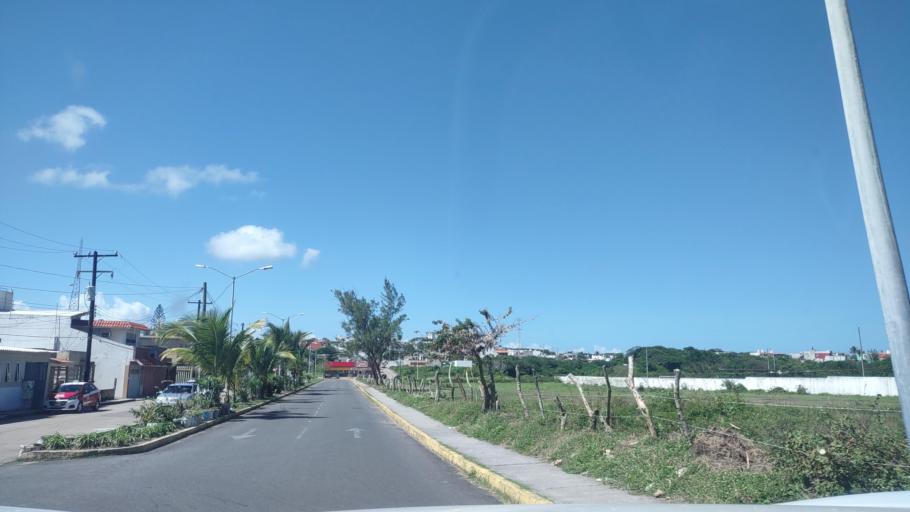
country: MX
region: Veracruz
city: Heroica Alvarado
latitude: 18.7817
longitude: -95.7684
